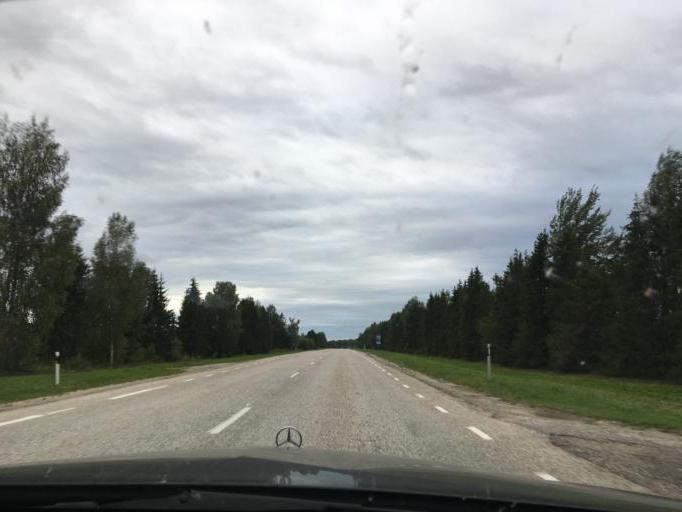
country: LV
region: Aluksnes Rajons
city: Aluksne
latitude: 57.6185
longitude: 27.2698
